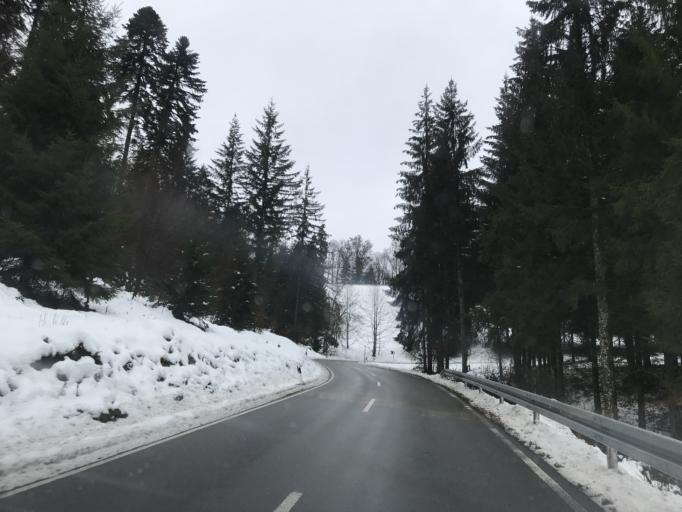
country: DE
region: Baden-Wuerttemberg
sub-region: Freiburg Region
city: Hasel
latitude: 47.6934
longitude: 7.8919
